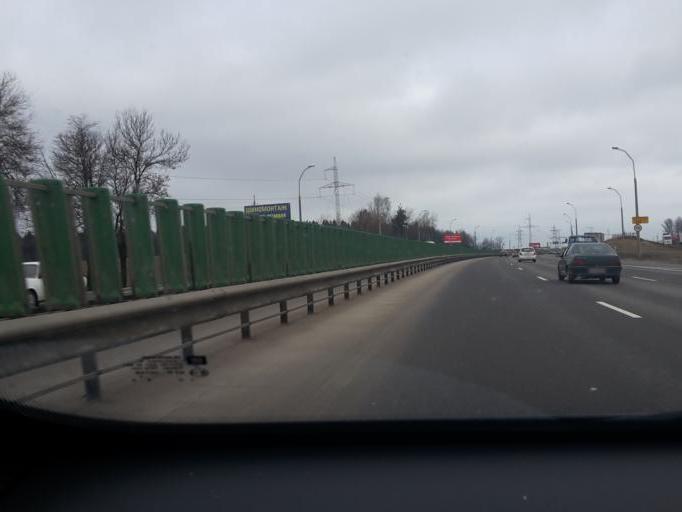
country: BY
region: Minsk
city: Zhdanovichy
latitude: 53.9032
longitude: 27.4071
